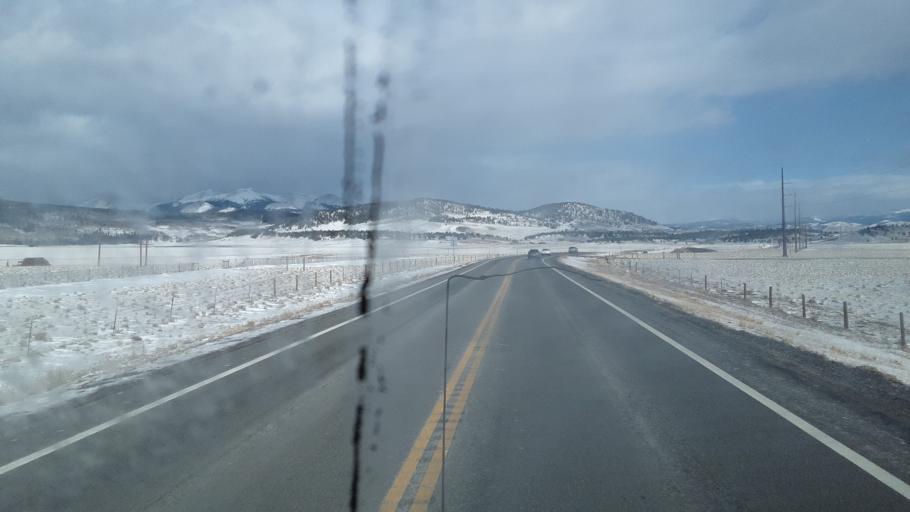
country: US
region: Colorado
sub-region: Park County
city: Fairplay
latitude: 39.2834
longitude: -105.9140
